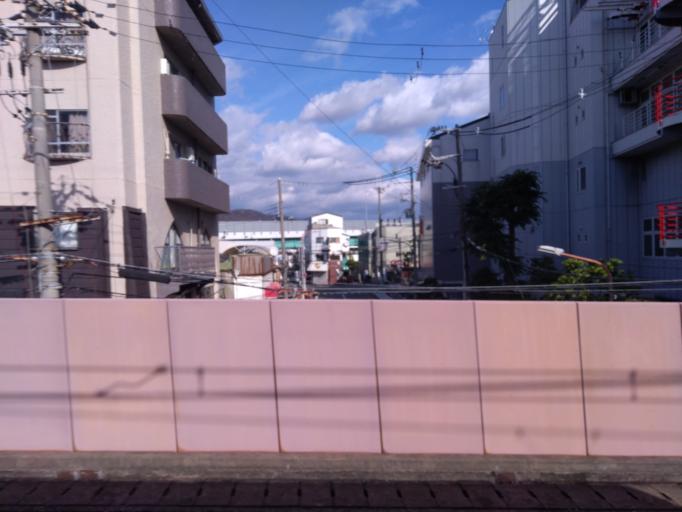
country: JP
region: Osaka
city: Ikeda
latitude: 34.8099
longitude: 135.4440
